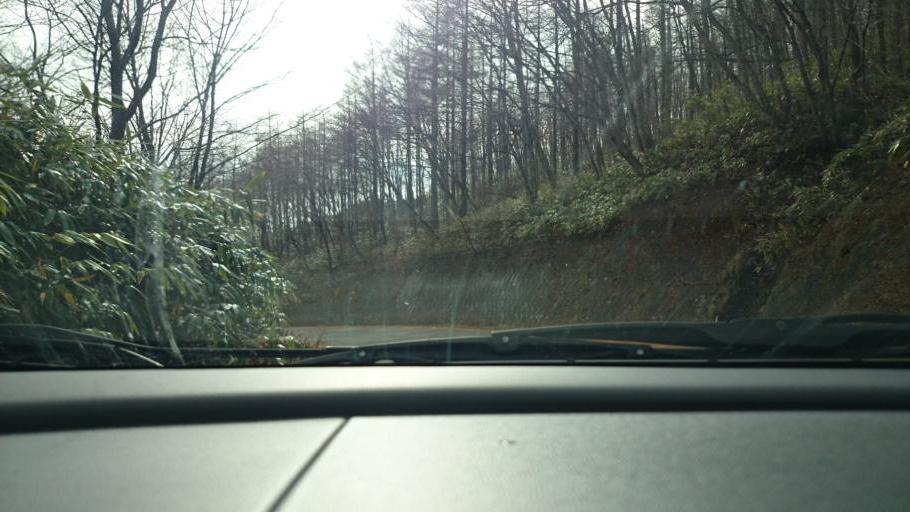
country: JP
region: Tochigi
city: Kuroiso
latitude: 37.1307
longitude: 140.0145
